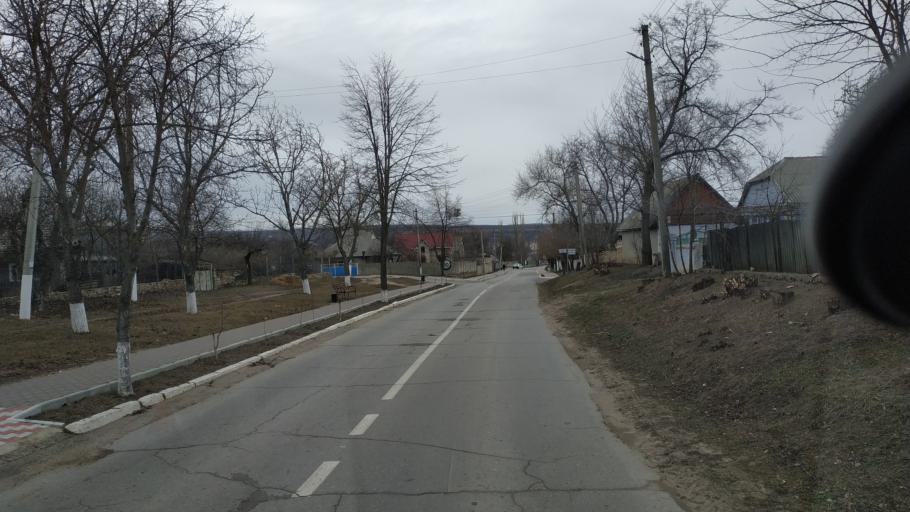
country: MD
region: Telenesti
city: Cocieri
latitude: 47.3444
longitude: 29.0925
